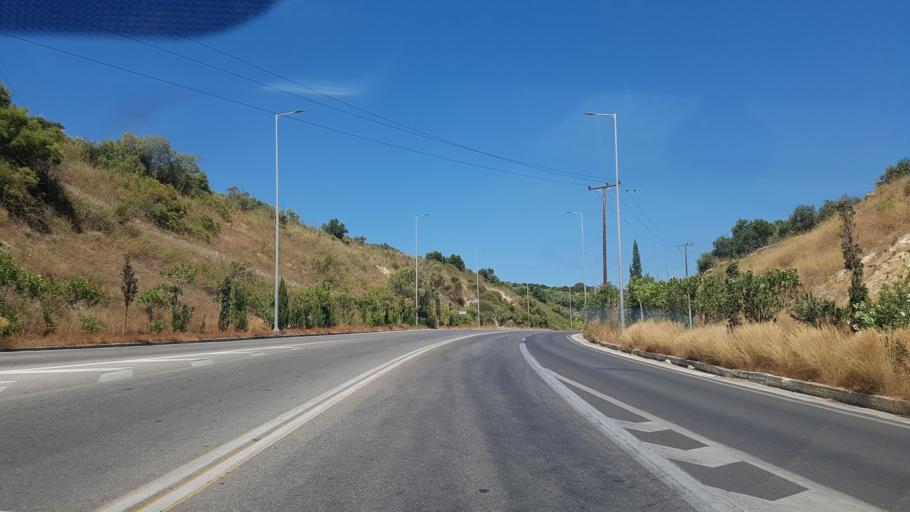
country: GR
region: Crete
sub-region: Nomos Chanias
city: Kolympari
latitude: 35.5301
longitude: 23.7816
